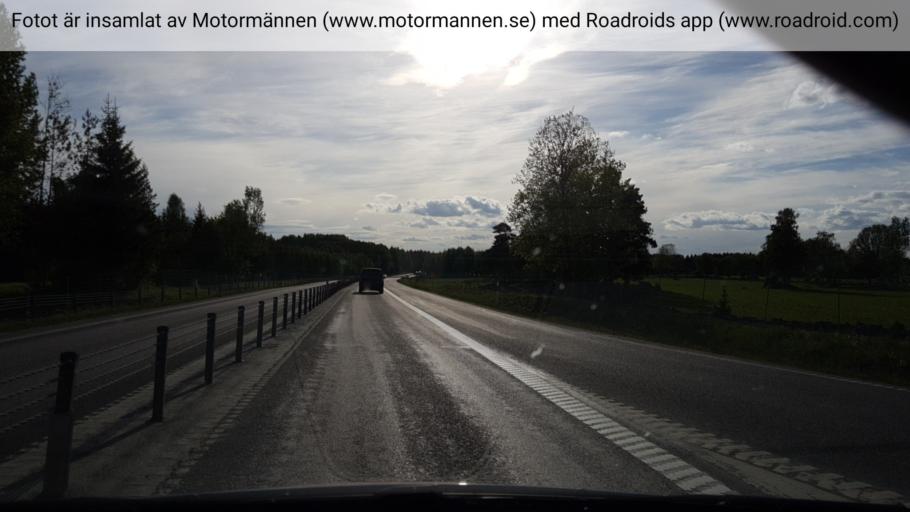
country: SE
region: Vaestmanland
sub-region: Hallstahammars Kommun
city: Kolback
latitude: 59.5793
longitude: 16.3205
